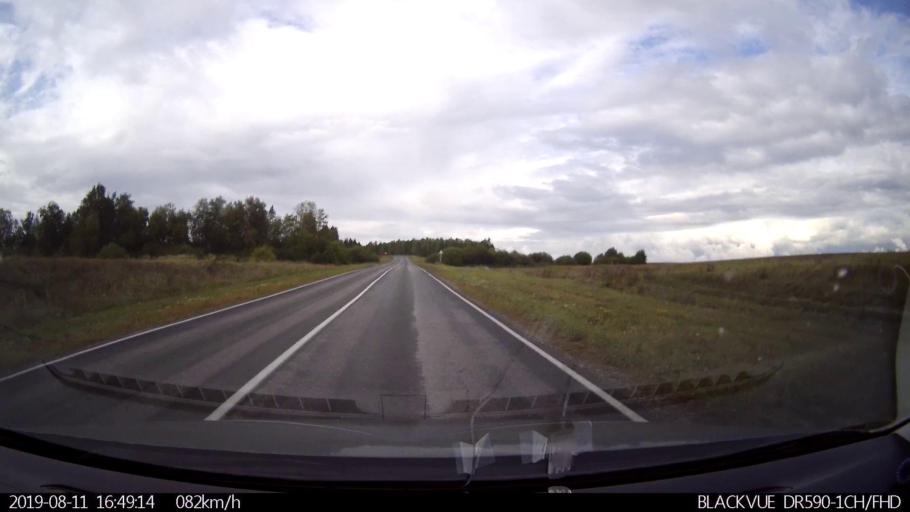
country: RU
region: Ulyanovsk
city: Mayna
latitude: 54.2187
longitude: 47.6951
